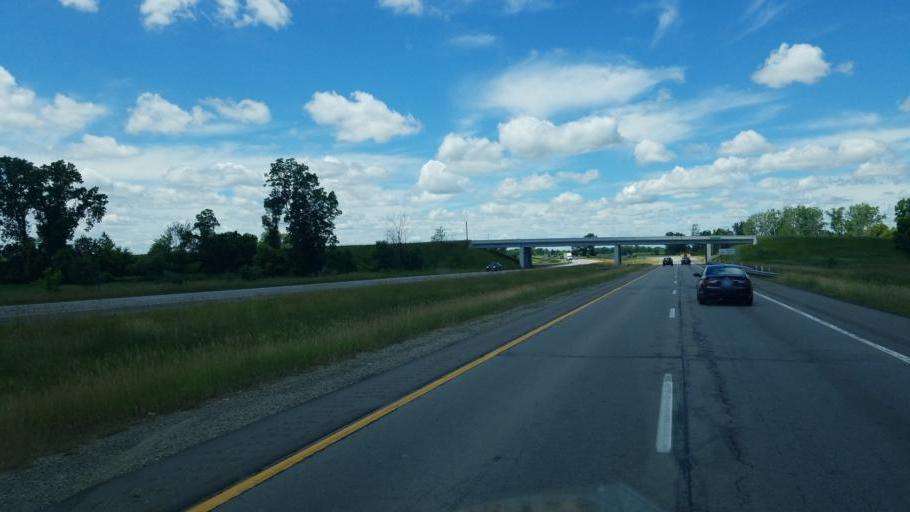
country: US
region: Michigan
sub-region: Livingston County
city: Fowlerville
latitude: 42.6493
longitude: -84.1098
